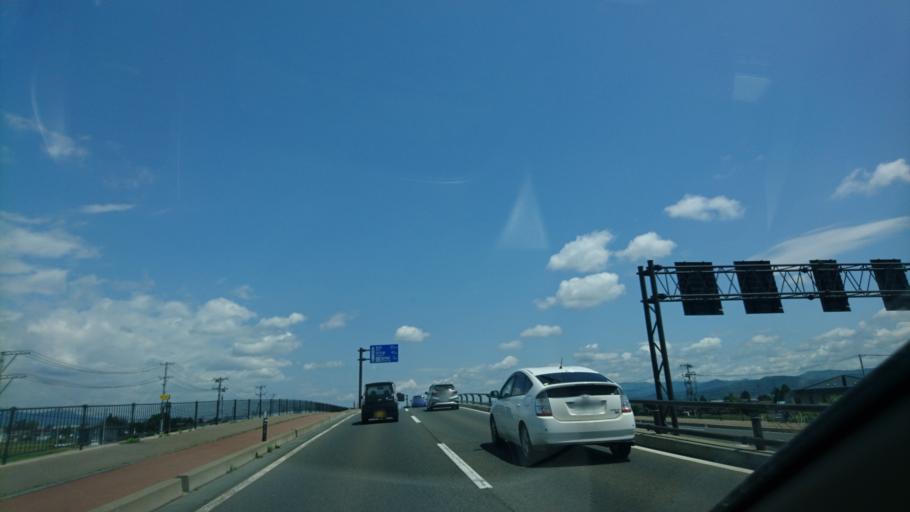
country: JP
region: Iwate
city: Morioka-shi
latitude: 39.6585
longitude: 141.1340
